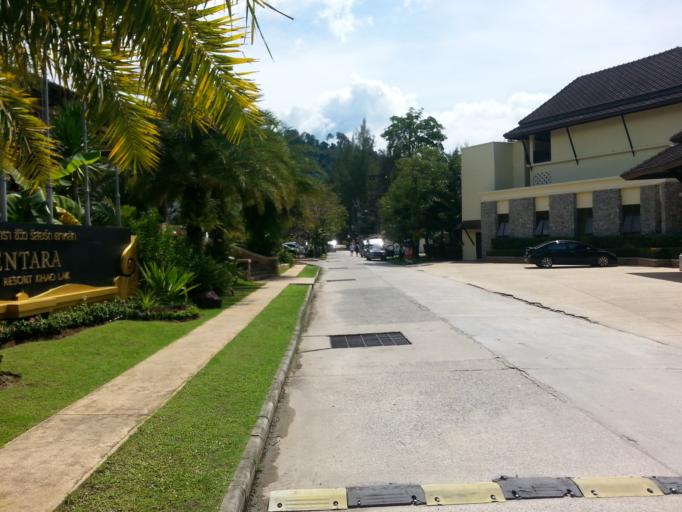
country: TH
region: Phangnga
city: Ban Khao Lak
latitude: 8.6429
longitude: 98.2475
